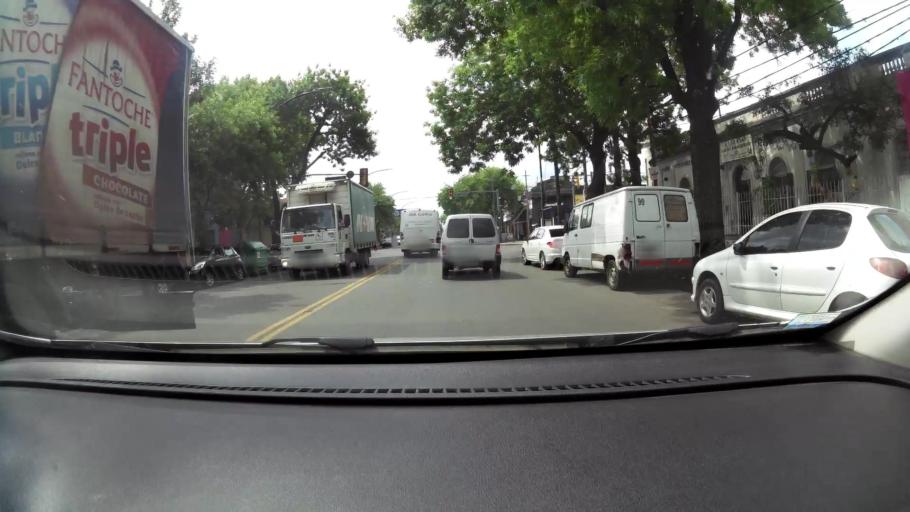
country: AR
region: Santa Fe
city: Gobernador Galvez
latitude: -33.0009
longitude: -60.6362
